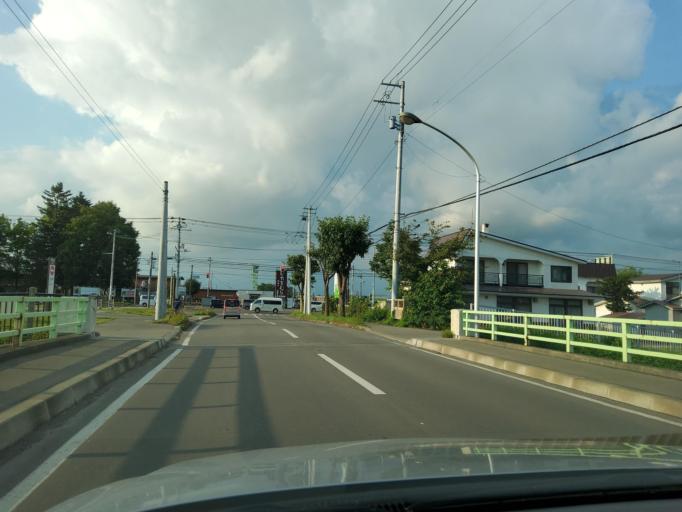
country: JP
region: Hokkaido
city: Obihiro
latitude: 42.9199
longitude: 143.1847
